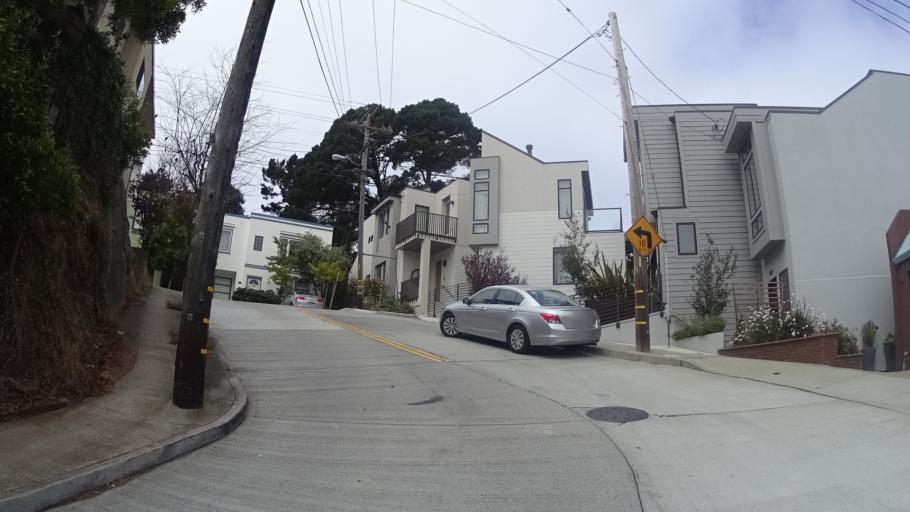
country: US
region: California
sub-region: San Mateo County
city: Daly City
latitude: 37.7354
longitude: -122.4417
